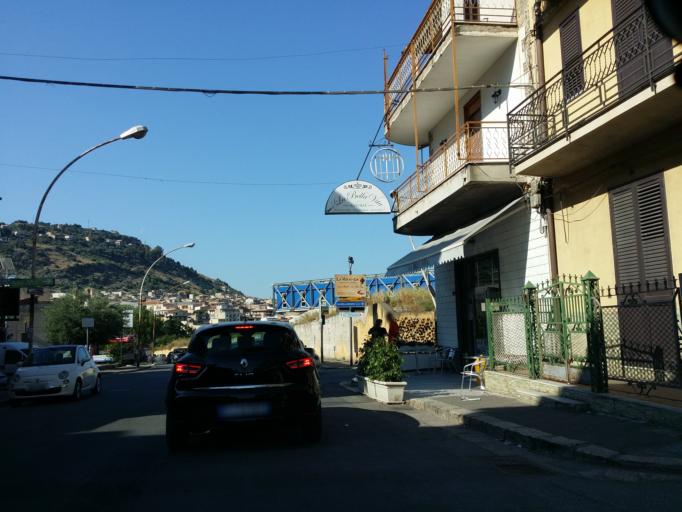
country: IT
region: Sicily
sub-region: Palermo
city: Misilmeri
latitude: 38.0288
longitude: 13.4492
